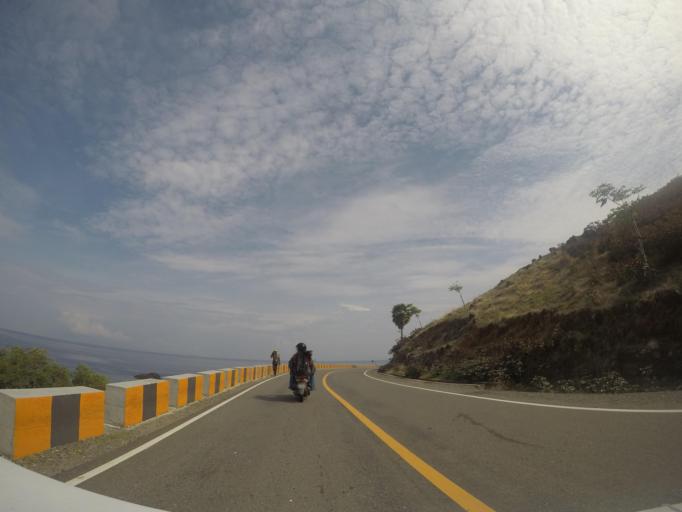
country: ID
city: Metinaro
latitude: -8.4800
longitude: 125.8433
